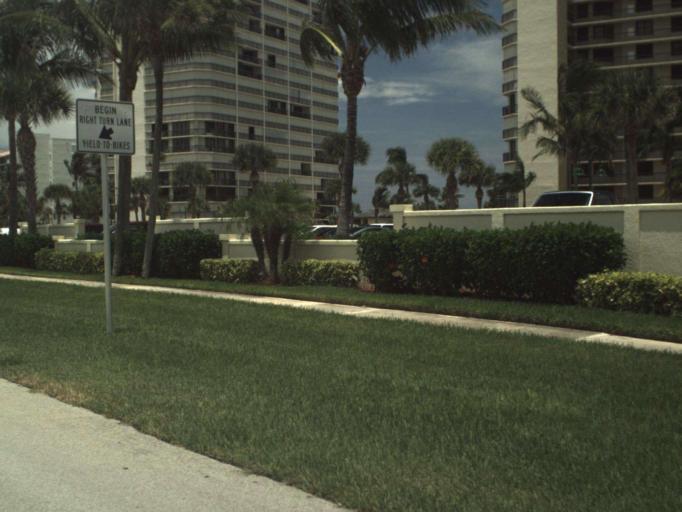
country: US
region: Florida
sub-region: Saint Lucie County
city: Hutchinson Island South
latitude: 27.2905
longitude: -80.2143
